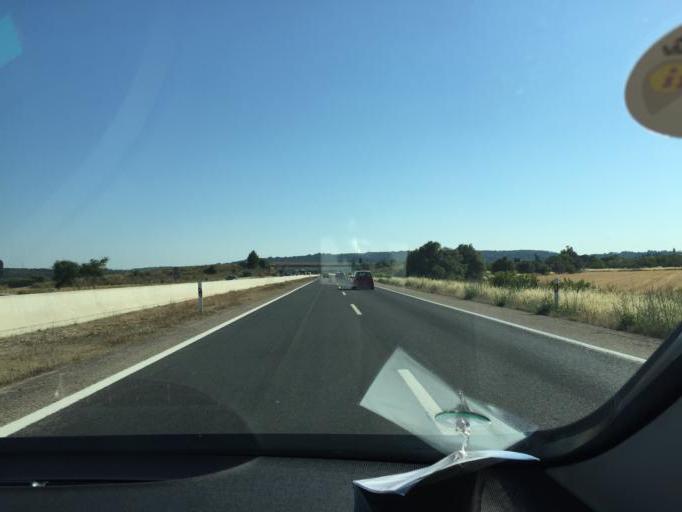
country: ES
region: Balearic Islands
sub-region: Illes Balears
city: Consell
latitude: 39.6529
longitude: 2.7993
